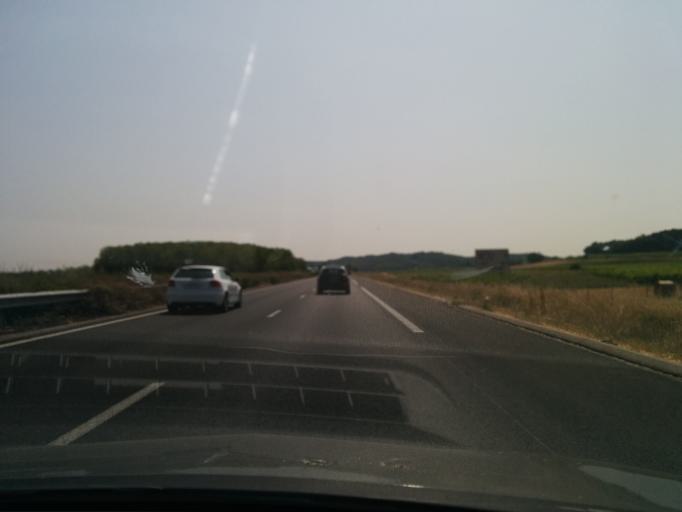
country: FR
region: Midi-Pyrenees
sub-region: Departement du Tarn
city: Lagrave
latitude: 43.8880
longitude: 1.9778
